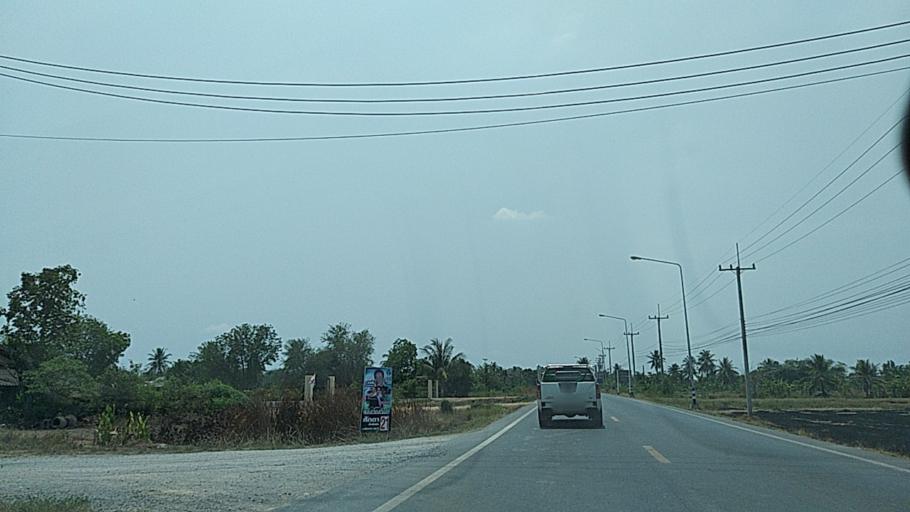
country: TH
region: Chachoengsao
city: Bang Nam Priao
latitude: 13.8710
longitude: 100.9671
